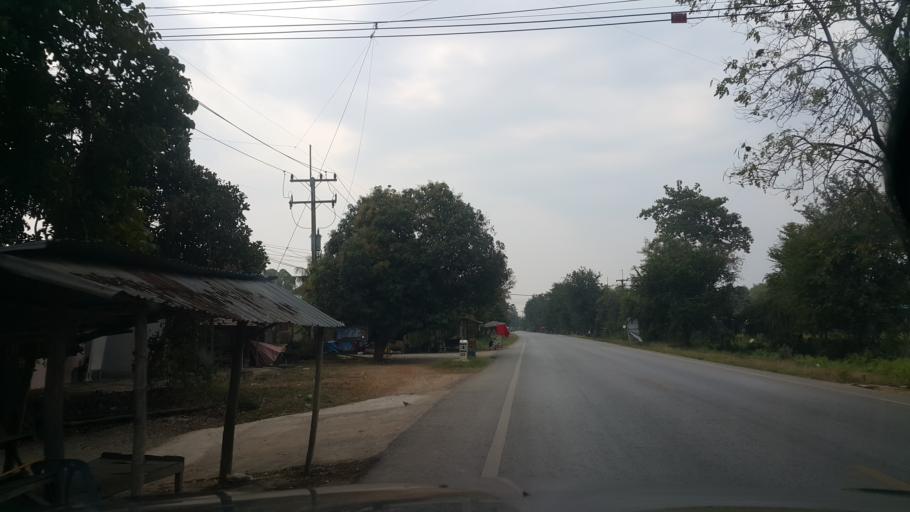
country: TH
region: Sukhothai
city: Si Samrong
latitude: 17.0994
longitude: 99.8857
